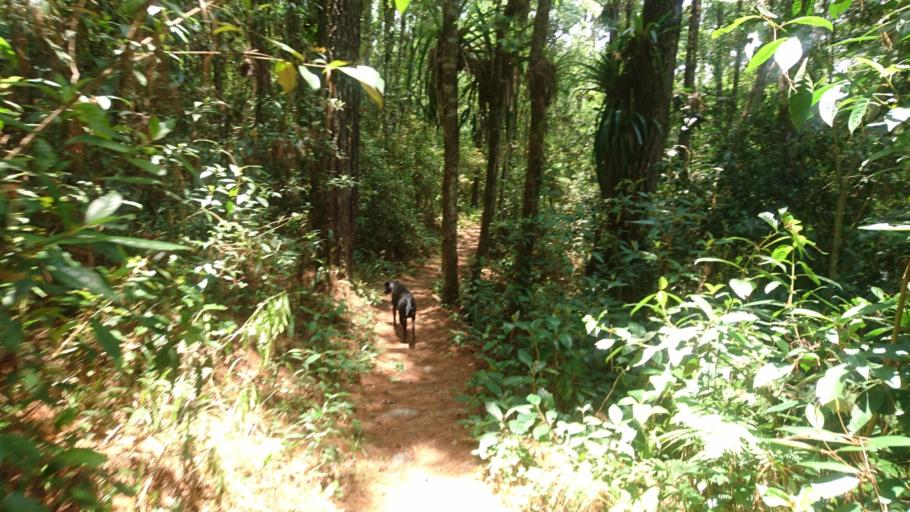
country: GT
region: Huehuetenango
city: Union
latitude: 16.1322
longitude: -91.7289
